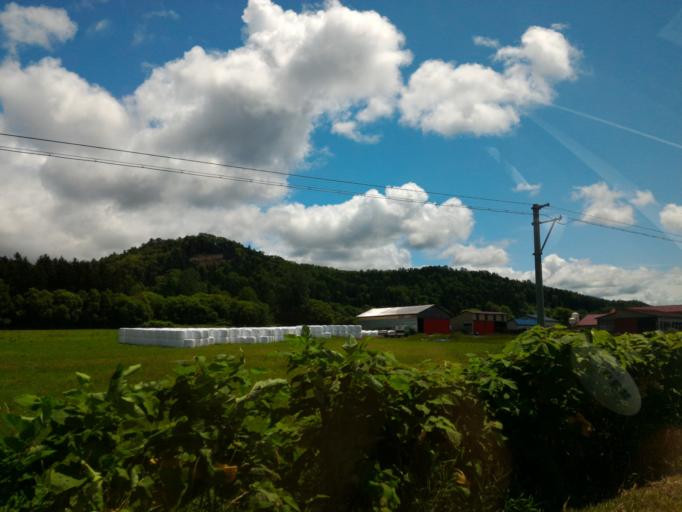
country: JP
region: Hokkaido
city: Nayoro
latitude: 44.5966
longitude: 142.3106
